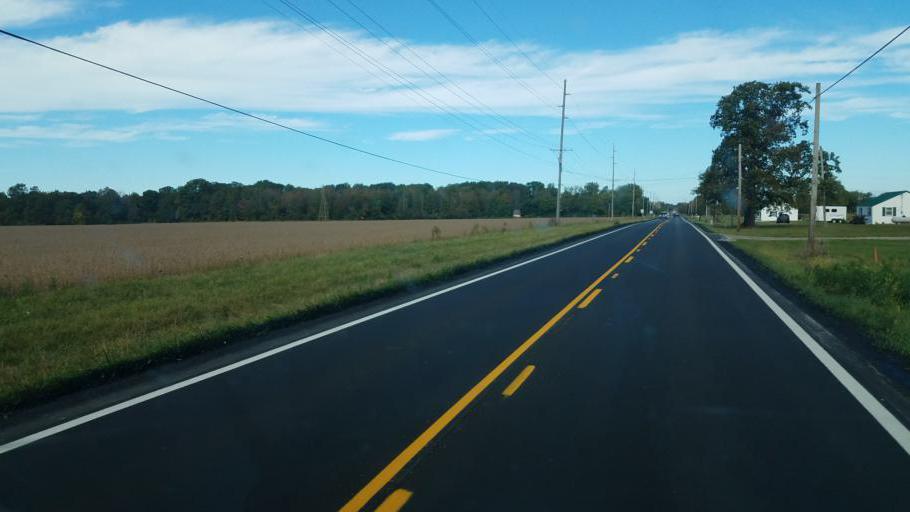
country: US
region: Ohio
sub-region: Erie County
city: Huron
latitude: 41.3539
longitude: -82.4940
